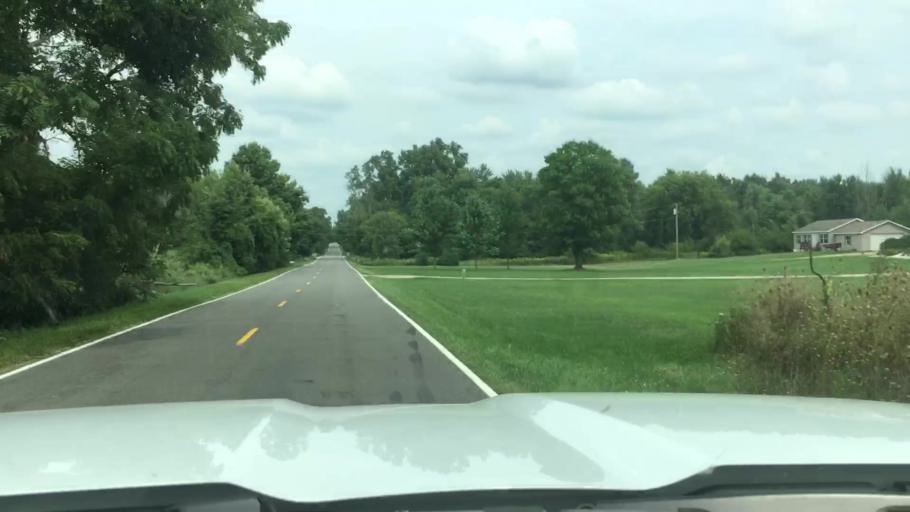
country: US
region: Michigan
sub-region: Ingham County
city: Webberville
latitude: 42.6792
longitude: -84.1894
